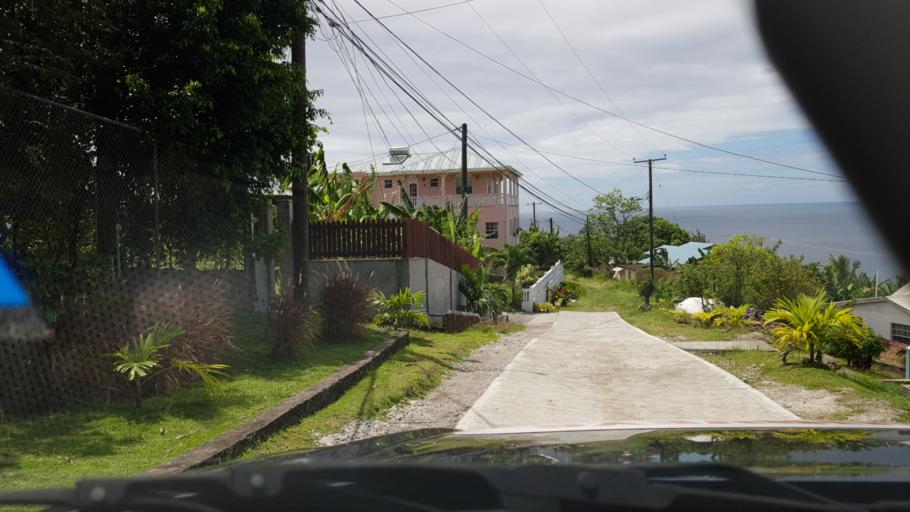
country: LC
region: Anse-la-Raye
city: Anse La Raye
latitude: 13.9446
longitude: -61.0405
